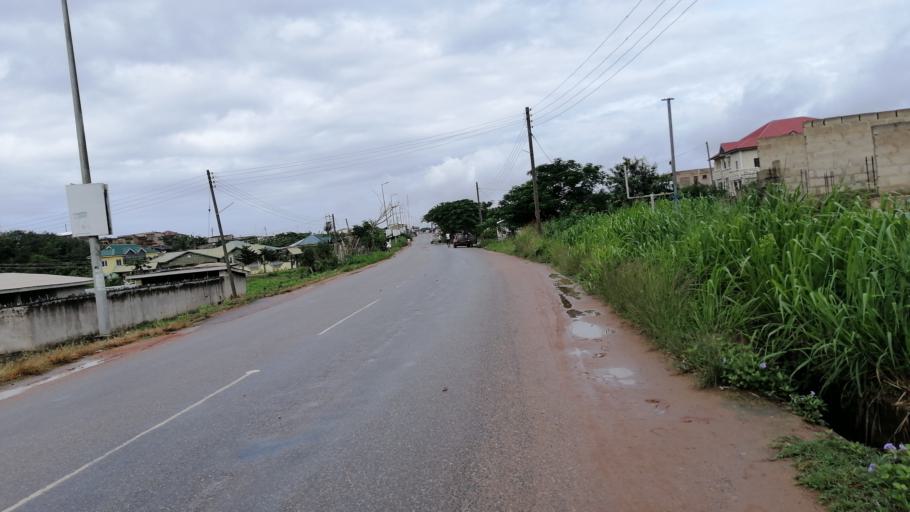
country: GH
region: Central
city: Cape Coast
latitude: 5.1488
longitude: -1.3014
